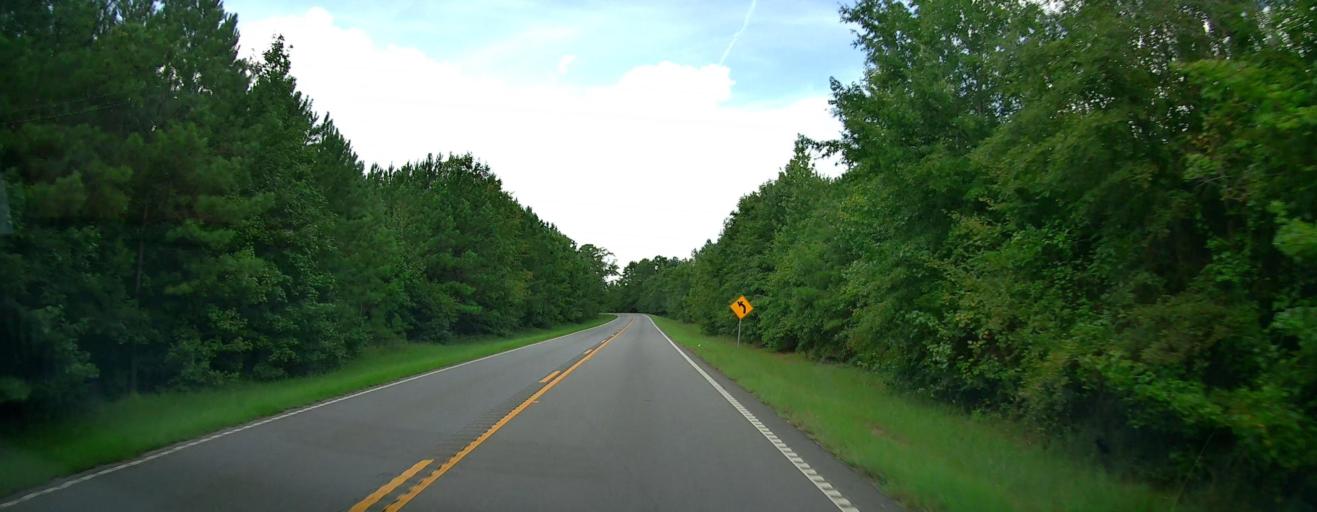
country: US
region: Georgia
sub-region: Talbot County
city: Talbotton
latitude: 32.6372
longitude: -84.4936
